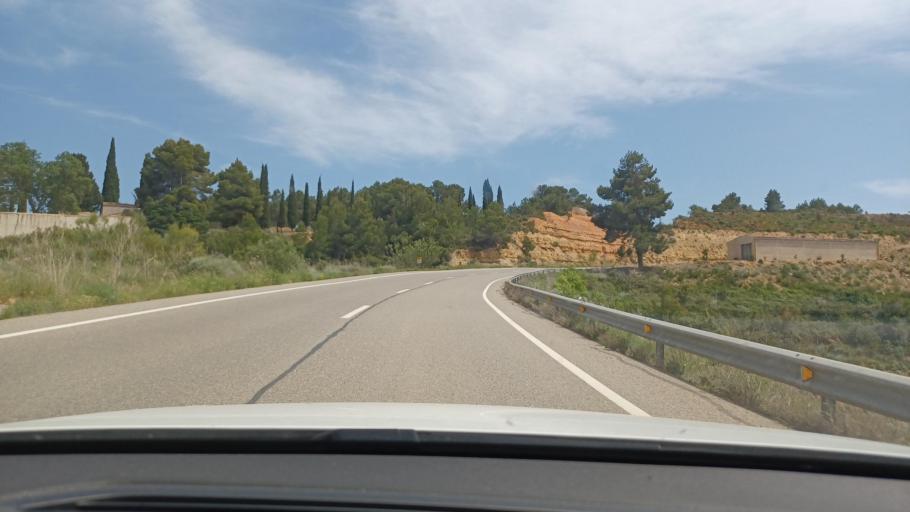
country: ES
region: Catalonia
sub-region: Provincia de Tarragona
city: Gandesa
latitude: 41.0622
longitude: 0.4368
